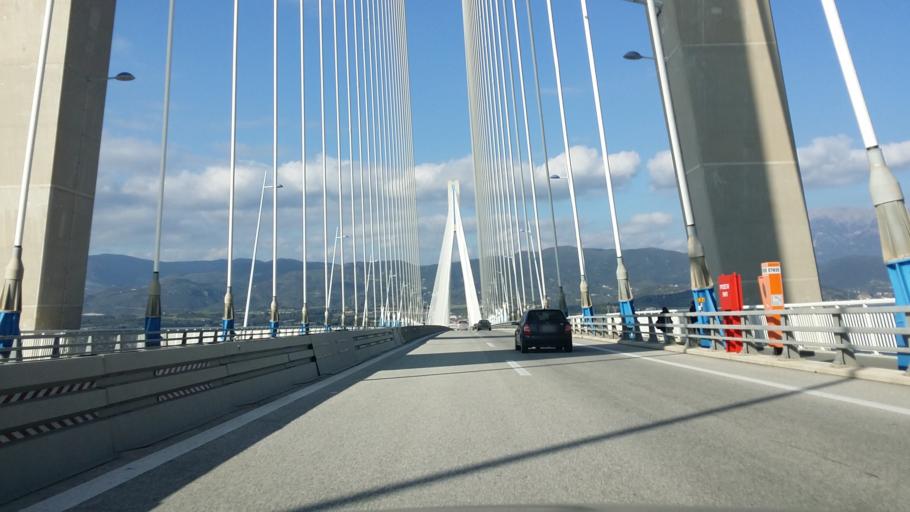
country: GR
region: West Greece
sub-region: Nomos Aitolias kai Akarnanias
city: Antirrio
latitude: 38.3224
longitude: 21.7722
